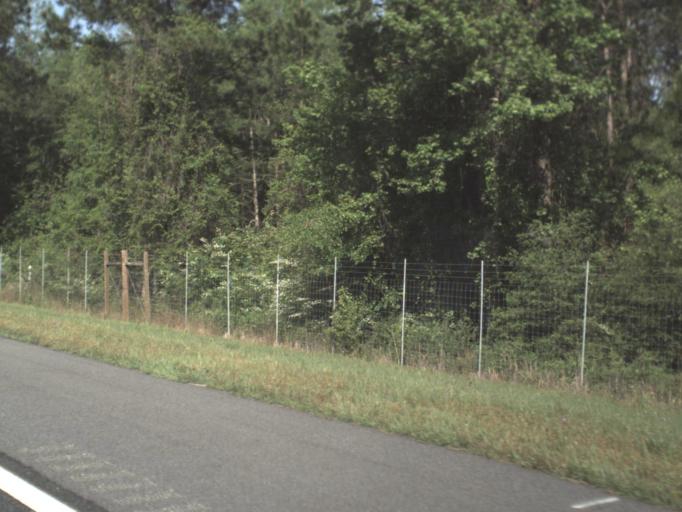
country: US
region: Florida
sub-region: Walton County
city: DeFuniak Springs
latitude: 30.7321
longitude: -85.8948
